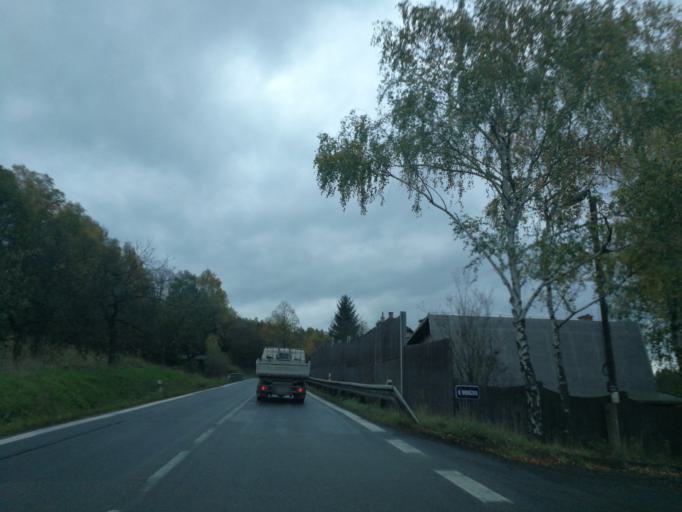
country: CZ
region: Zlin
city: Valasske Mezirici
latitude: 49.5020
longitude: 17.9940
